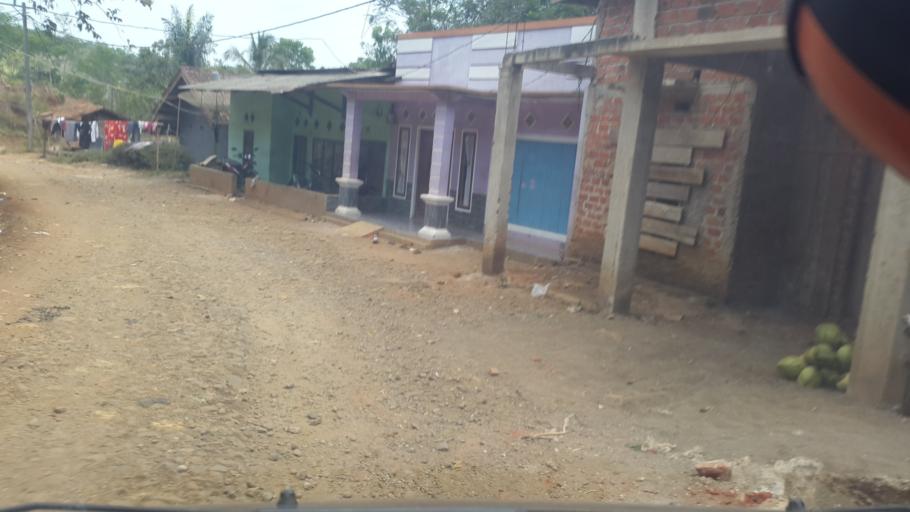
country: ID
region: West Java
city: Cisireum
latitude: -7.0999
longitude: 106.6522
